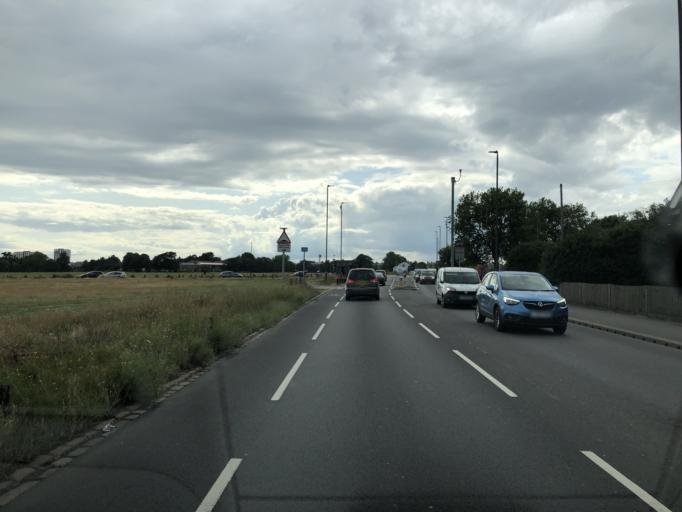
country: GB
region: England
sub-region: Greater London
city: Blackheath
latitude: 51.4719
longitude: 0.0011
